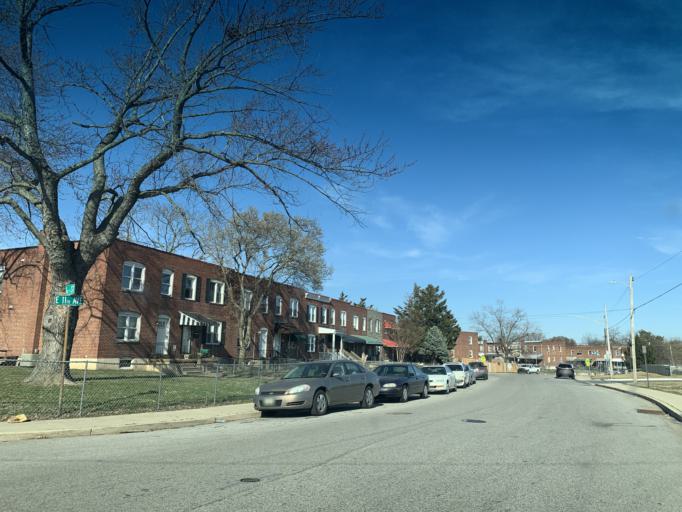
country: US
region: Maryland
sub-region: Anne Arundel County
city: Brooklyn Park
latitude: 39.2239
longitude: -76.6116
